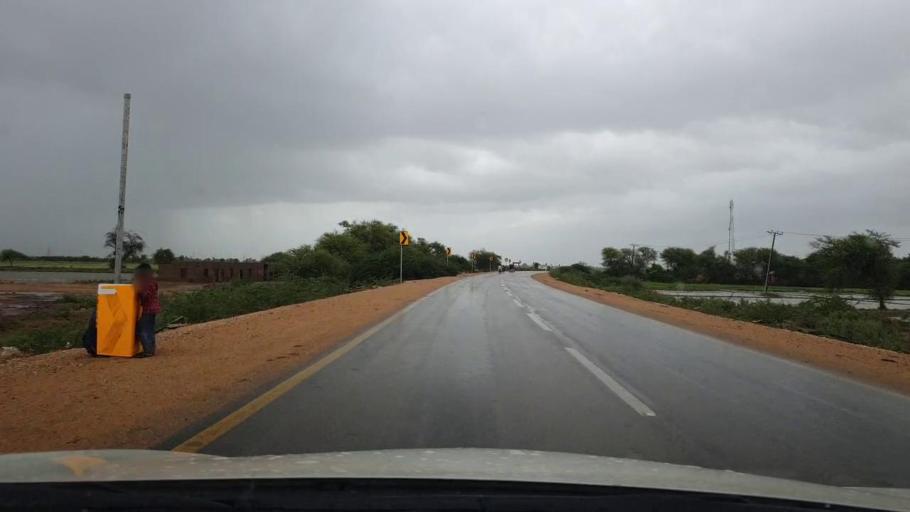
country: PK
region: Sindh
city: Kario
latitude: 24.6539
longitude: 68.6606
